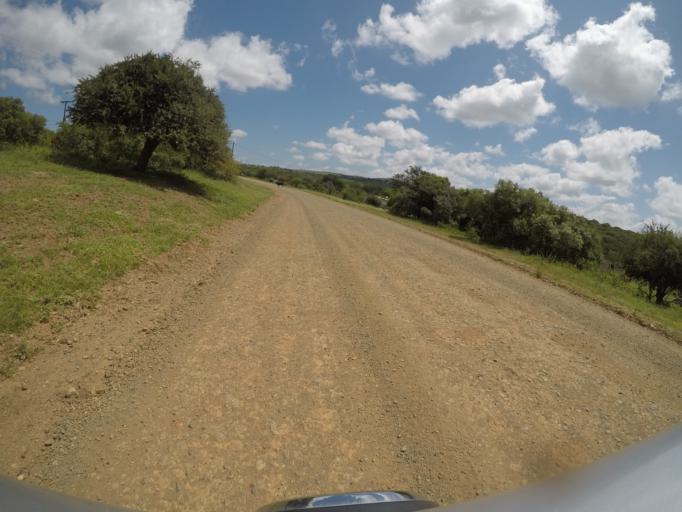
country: ZA
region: KwaZulu-Natal
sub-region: uThungulu District Municipality
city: Empangeni
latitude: -28.5943
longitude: 31.8326
